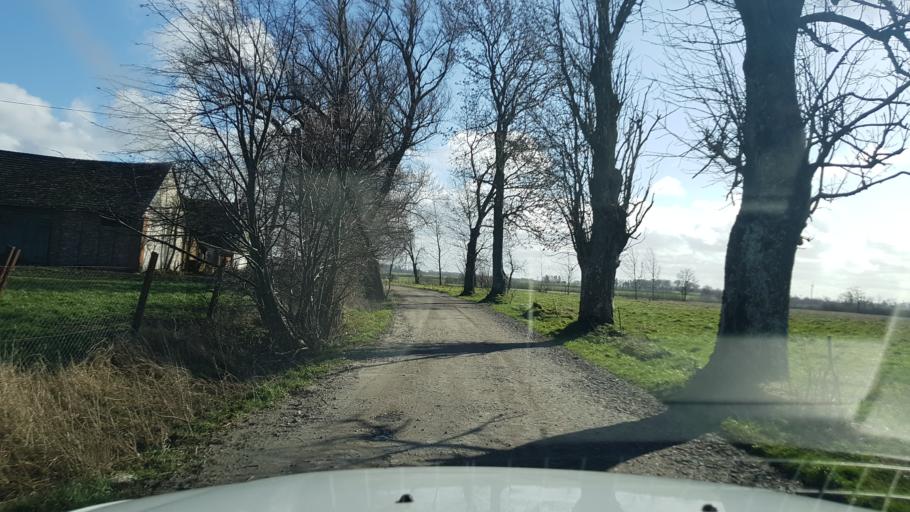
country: PL
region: West Pomeranian Voivodeship
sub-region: Powiat slawienski
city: Slawno
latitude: 54.3626
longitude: 16.5827
